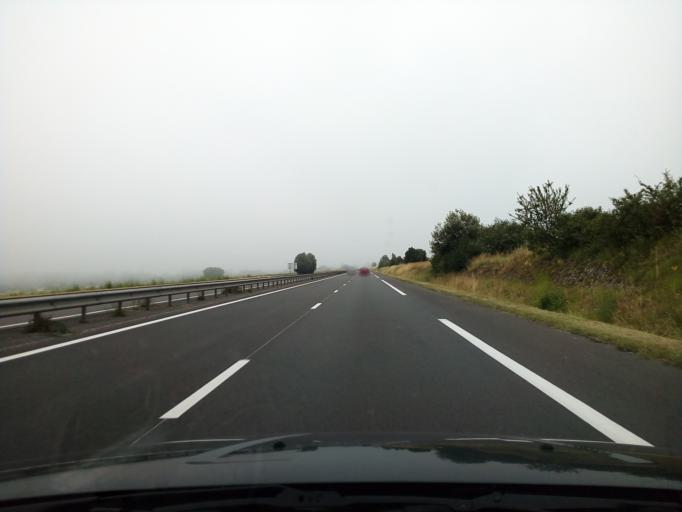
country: FR
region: Poitou-Charentes
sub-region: Departement de la Charente
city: Gensac-la-Pallue
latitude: 45.6677
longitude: -0.2460
